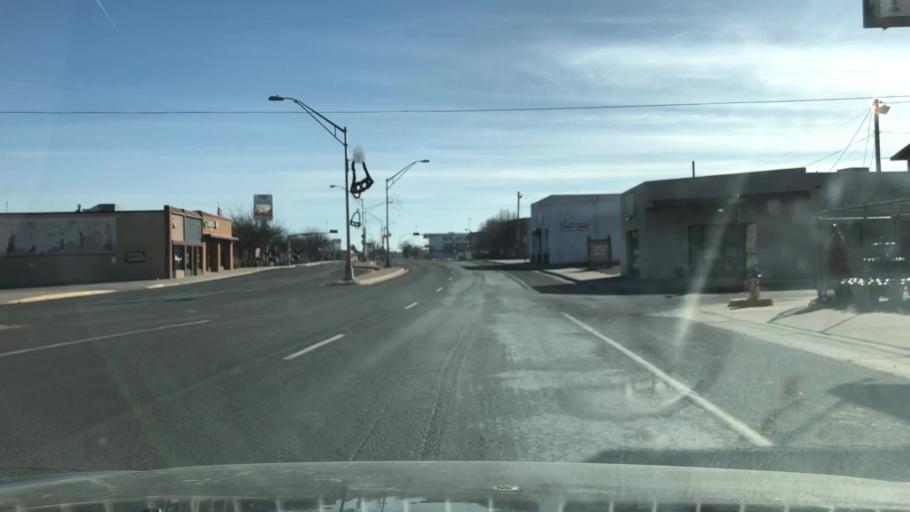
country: US
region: New Mexico
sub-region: Socorro County
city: Socorro
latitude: 34.0587
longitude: -106.8918
